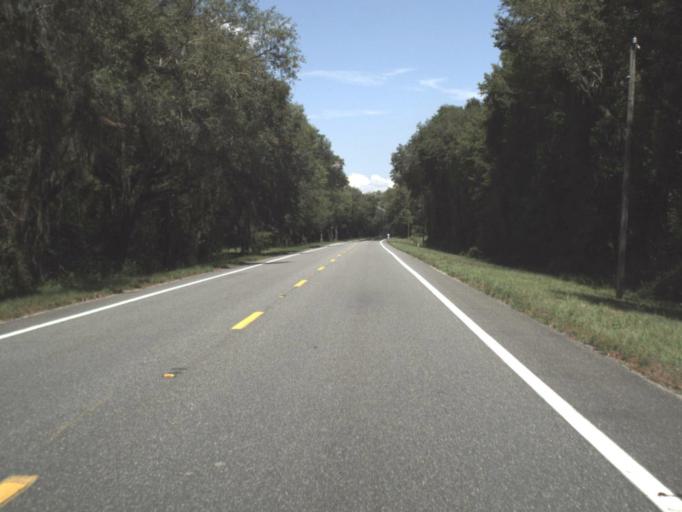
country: US
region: Florida
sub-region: Lafayette County
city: Mayo
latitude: 30.1294
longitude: -83.3207
